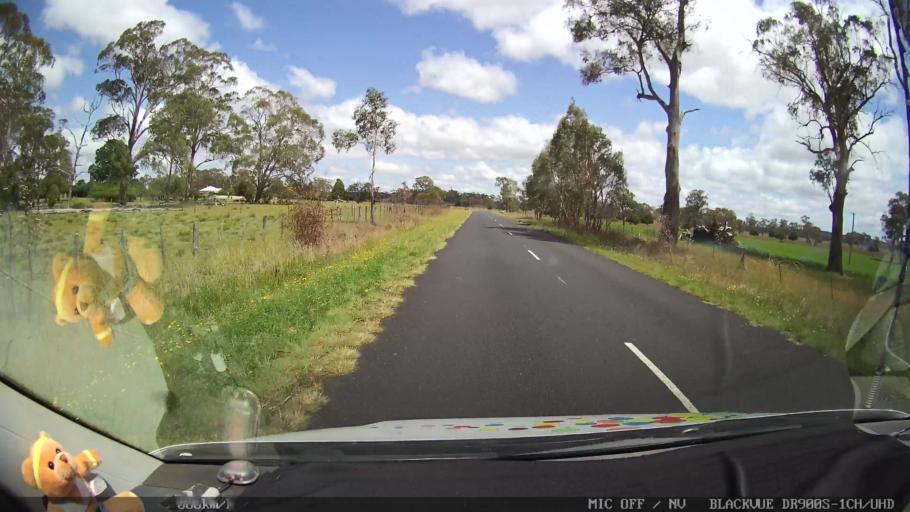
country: AU
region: New South Wales
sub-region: Glen Innes Severn
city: Glen Innes
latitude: -29.6304
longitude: 151.6756
